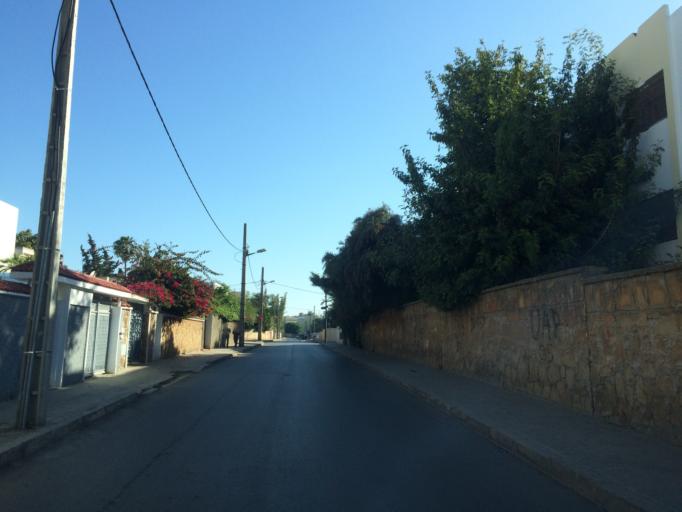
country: MA
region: Rabat-Sale-Zemmour-Zaer
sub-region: Rabat
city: Rabat
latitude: 33.9922
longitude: -6.8207
